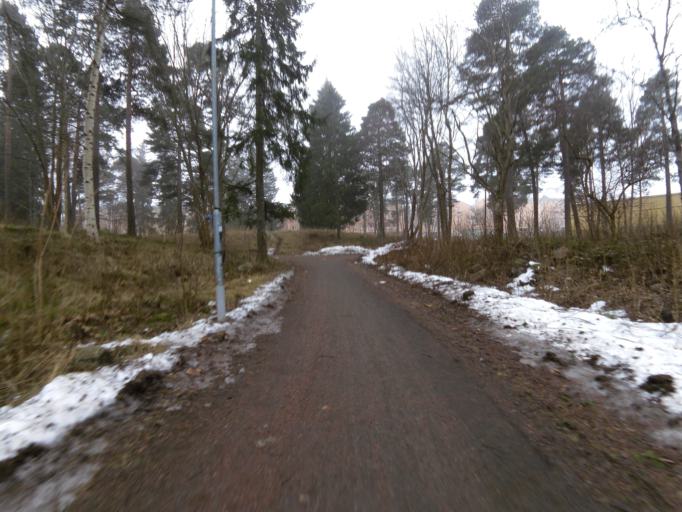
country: SE
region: Gaevleborg
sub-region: Gavle Kommun
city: Gavle
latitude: 60.6614
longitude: 17.1458
